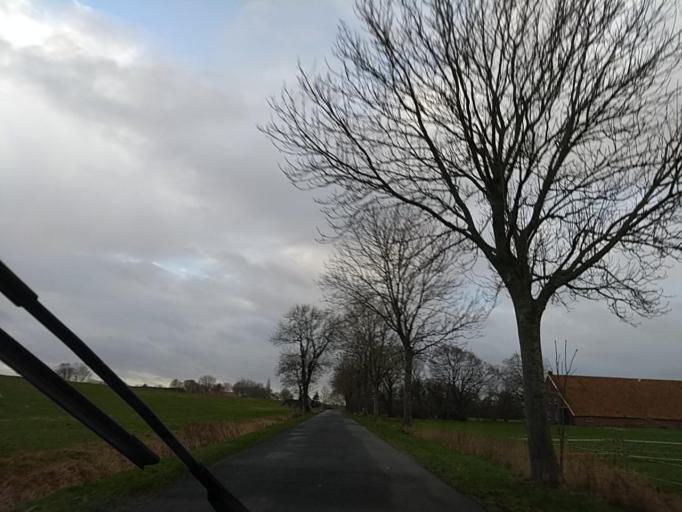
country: DE
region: Lower Saxony
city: Bunde
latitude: 53.2380
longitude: 7.2326
